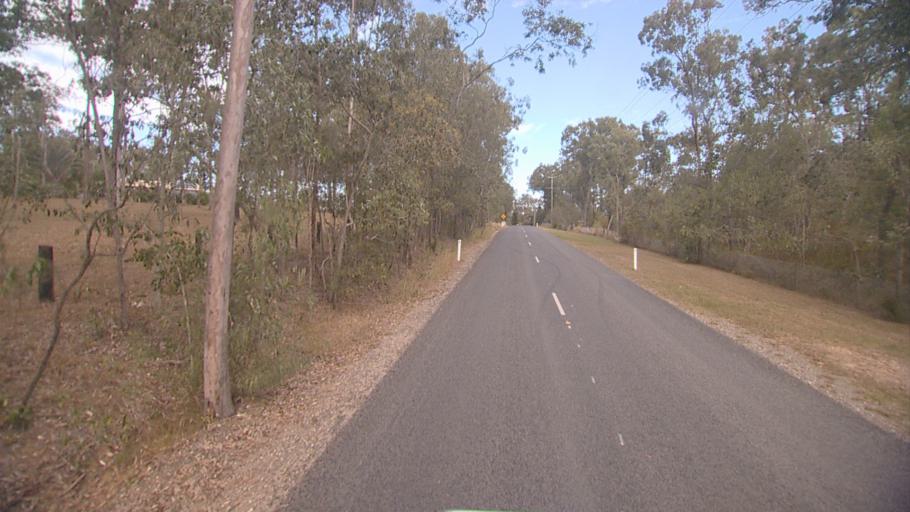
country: AU
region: Queensland
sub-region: Logan
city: North Maclean
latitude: -27.7629
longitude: 152.9704
